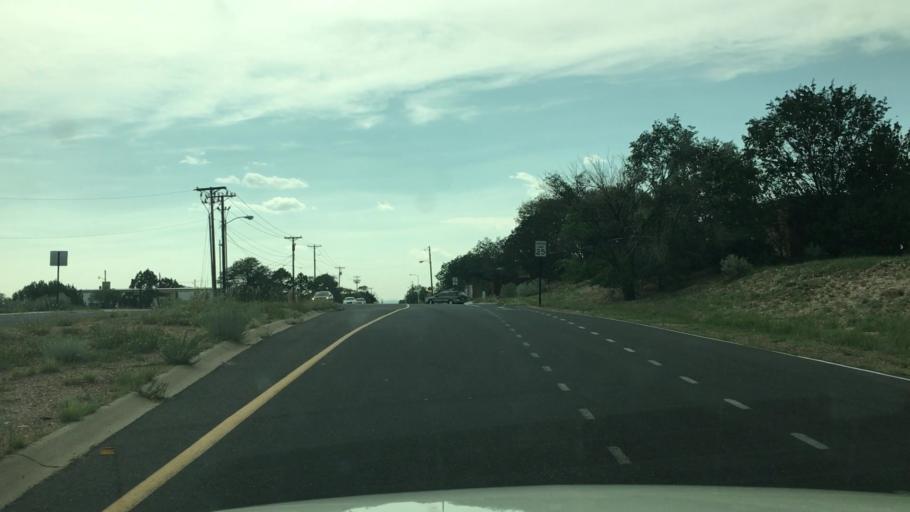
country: US
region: New Mexico
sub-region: Santa Fe County
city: Santa Fe
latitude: 35.6522
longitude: -105.9576
